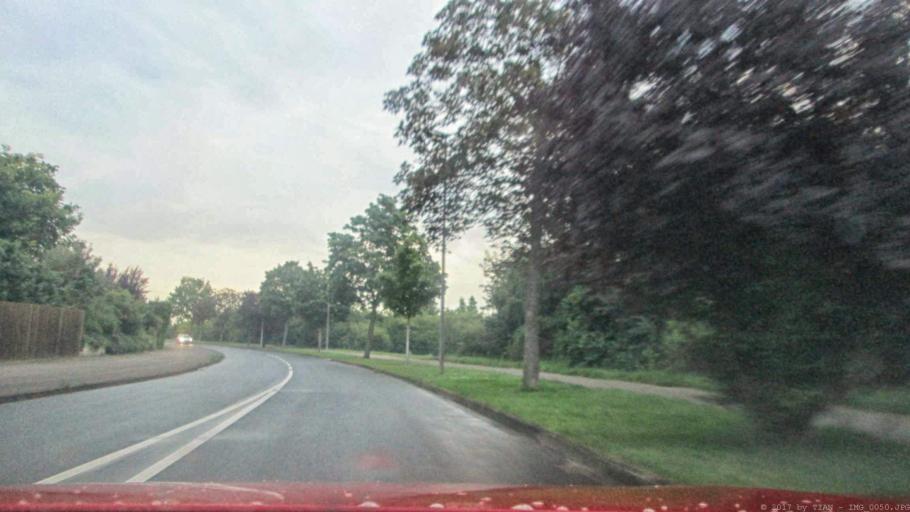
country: DE
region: Lower Saxony
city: Weyhausen
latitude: 52.4115
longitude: 10.7292
